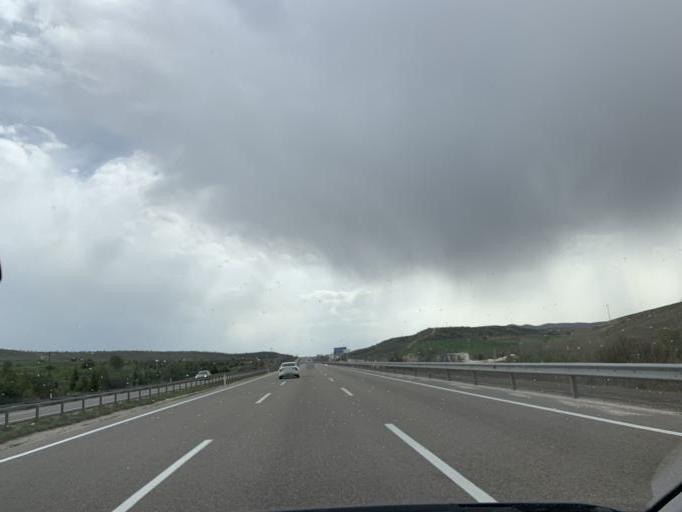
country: TR
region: Eskisehir
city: Sivrihisar
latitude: 39.5205
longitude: 31.6207
